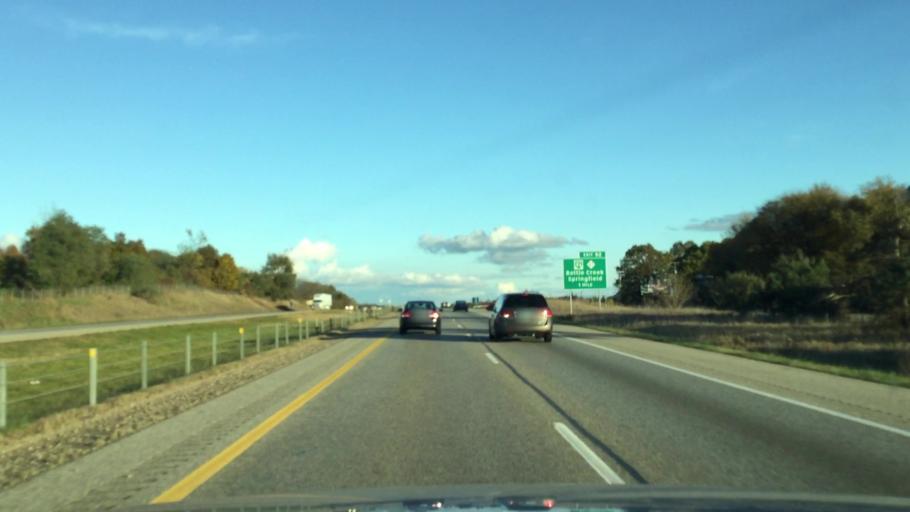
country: US
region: Michigan
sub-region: Calhoun County
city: Springfield
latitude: 42.2762
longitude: -85.3155
